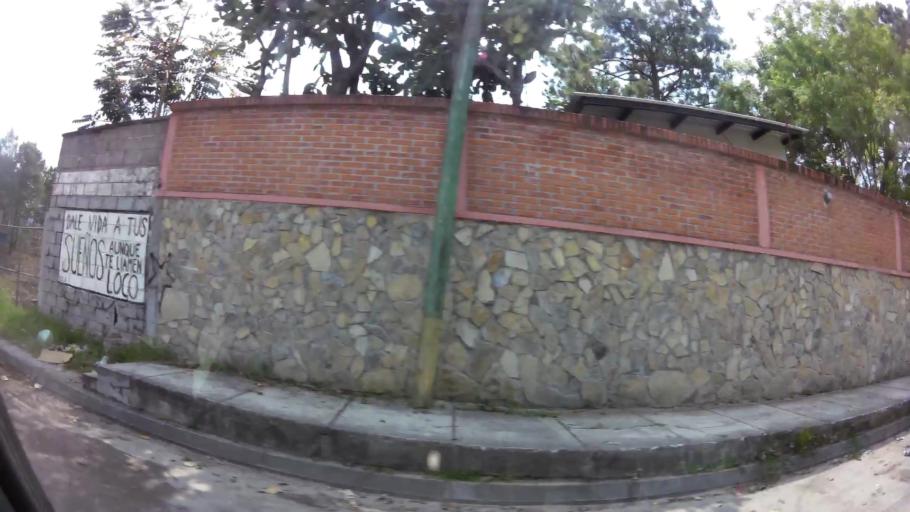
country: HN
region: Comayagua
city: Siguatepeque
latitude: 14.6086
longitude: -87.8302
